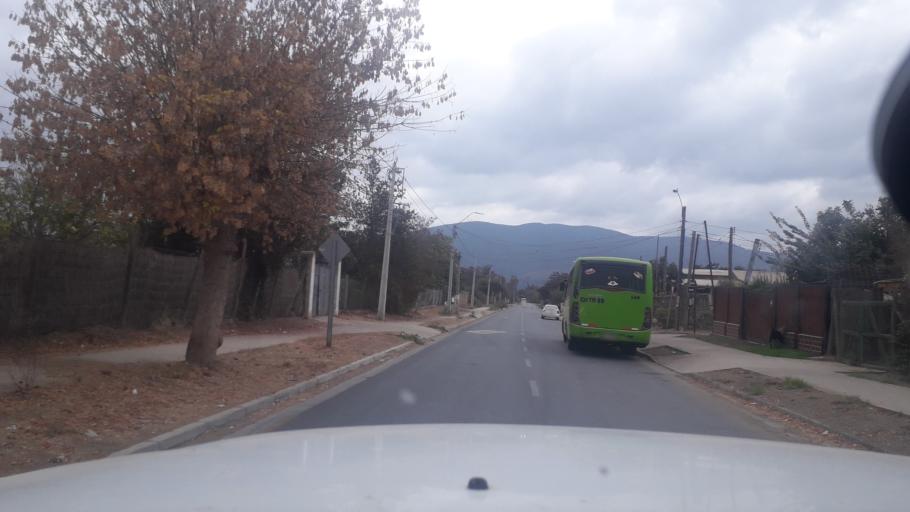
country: CL
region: Valparaiso
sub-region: Provincia de Marga Marga
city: Limache
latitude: -33.0179
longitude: -71.2691
